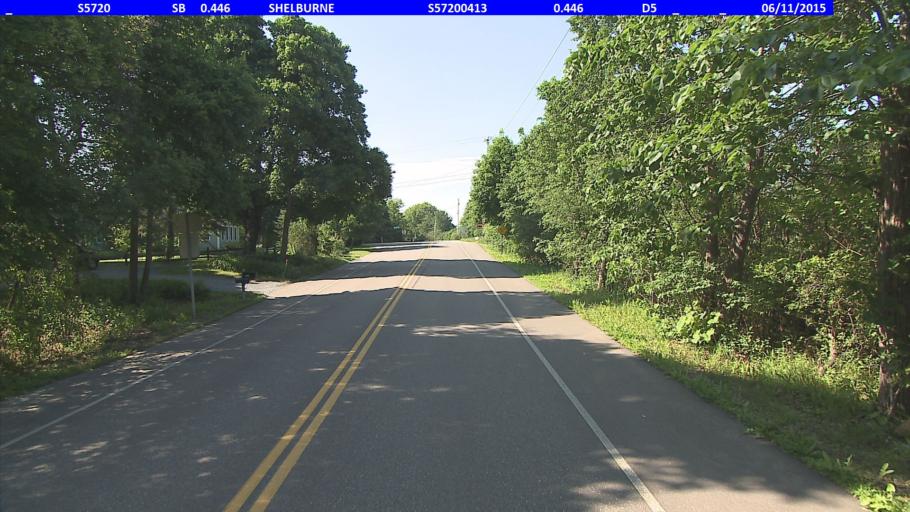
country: US
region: Vermont
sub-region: Chittenden County
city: South Burlington
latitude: 44.3745
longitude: -73.2024
